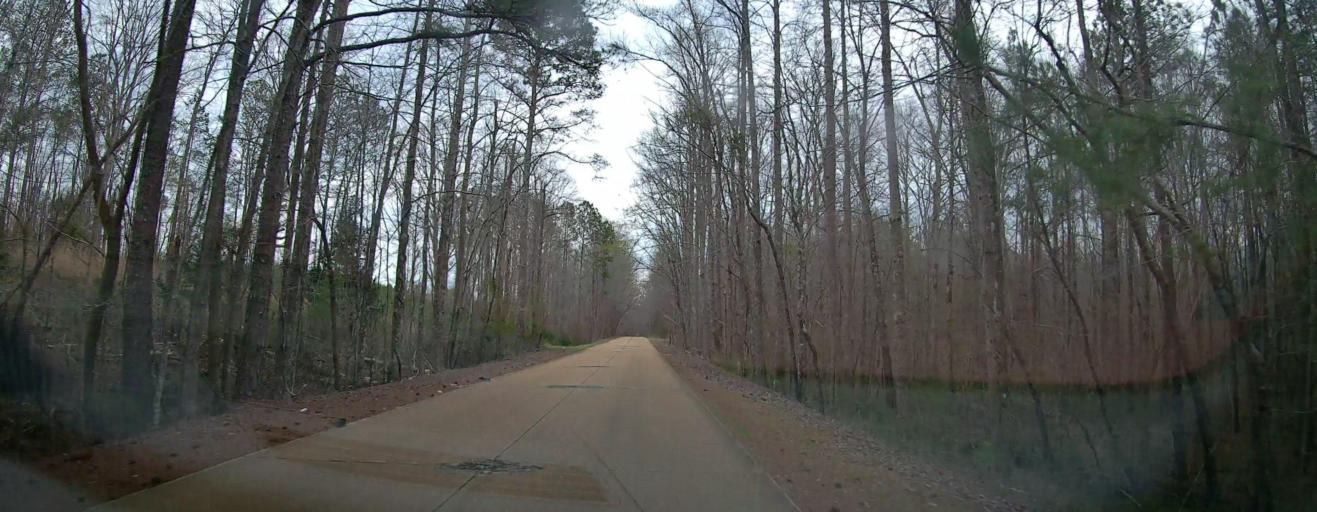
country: US
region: Alabama
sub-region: Marion County
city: Hamilton
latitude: 34.2050
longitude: -88.1926
